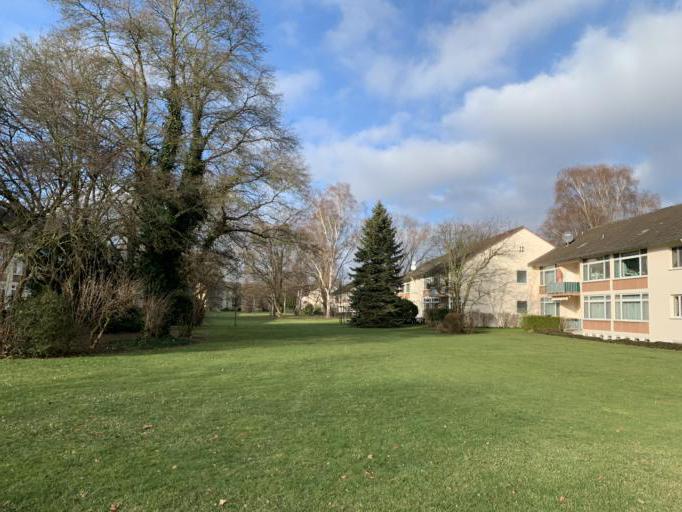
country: DE
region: North Rhine-Westphalia
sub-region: Regierungsbezirk Koln
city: Konigswinter
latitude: 50.7055
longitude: 7.1584
